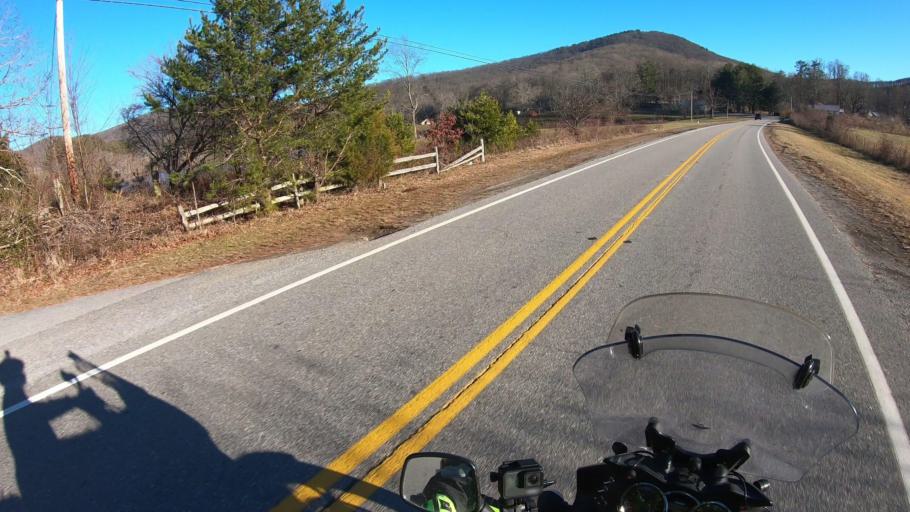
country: US
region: Georgia
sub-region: Lumpkin County
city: Dahlonega
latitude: 34.6963
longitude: -84.0252
